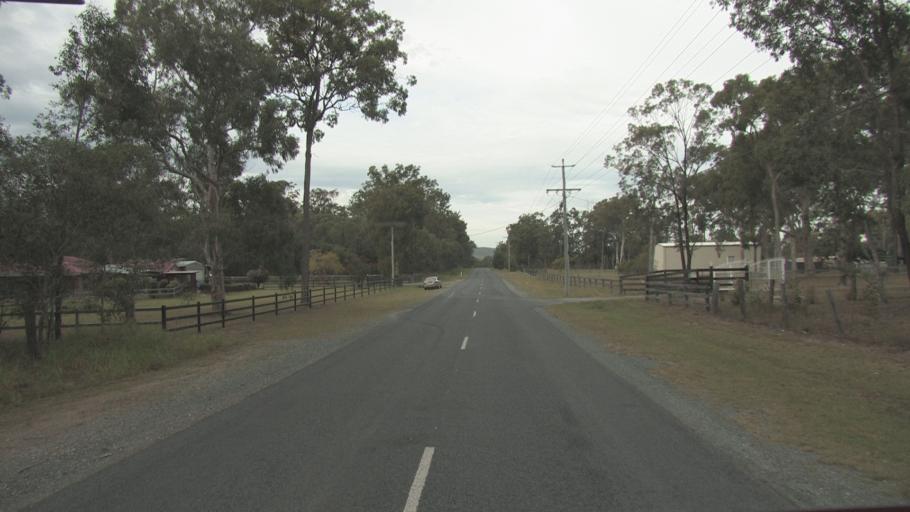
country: AU
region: Queensland
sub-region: Logan
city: Chambers Flat
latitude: -27.7841
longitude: 153.1148
